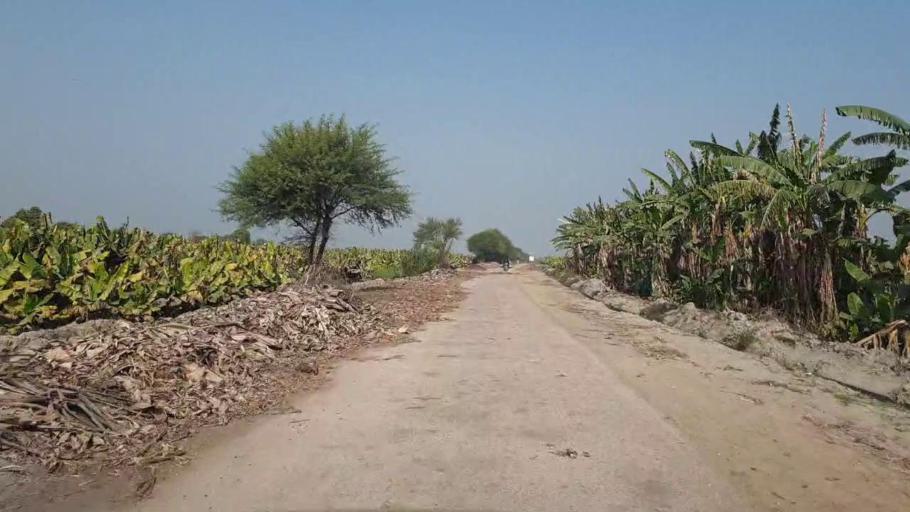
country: PK
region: Sindh
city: Bhit Shah
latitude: 25.7795
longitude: 68.4937
